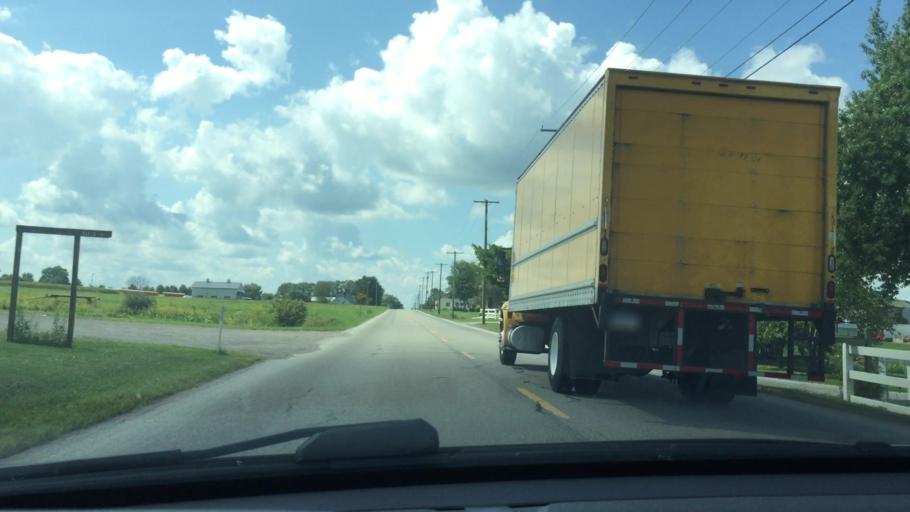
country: US
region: Pennsylvania
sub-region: Lawrence County
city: New Wilmington
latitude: 41.1204
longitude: -80.3660
